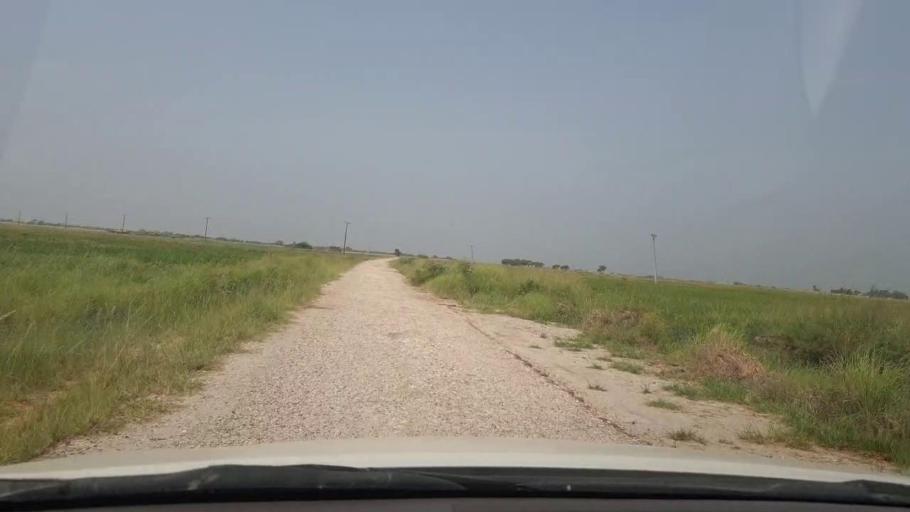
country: PK
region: Sindh
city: Shikarpur
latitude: 28.0240
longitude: 68.6118
